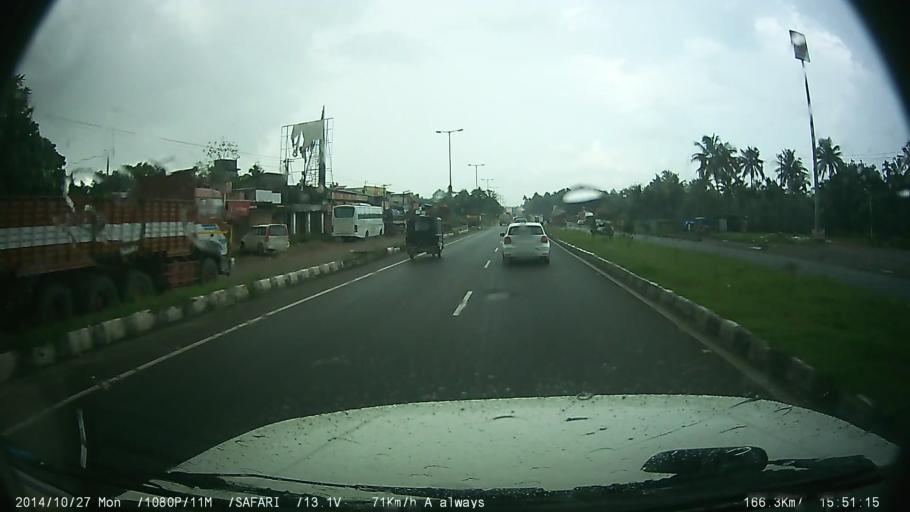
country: IN
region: Kerala
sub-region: Ernakulam
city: Angamali
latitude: 10.2487
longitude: 76.3692
